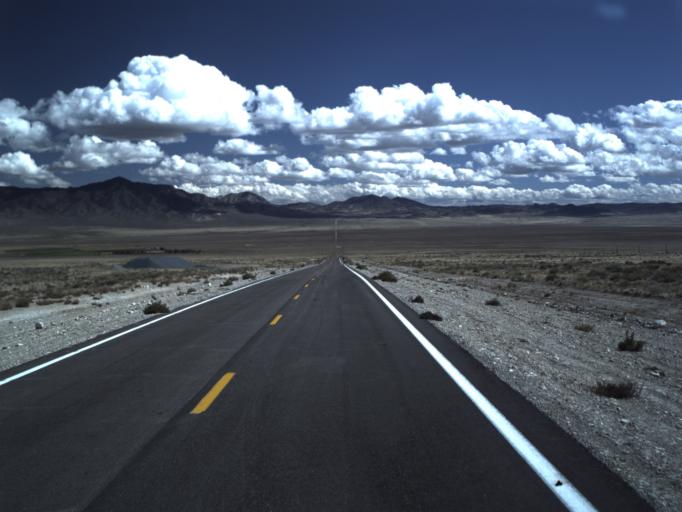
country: US
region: Utah
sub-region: Beaver County
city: Milford
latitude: 38.4940
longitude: -113.4792
